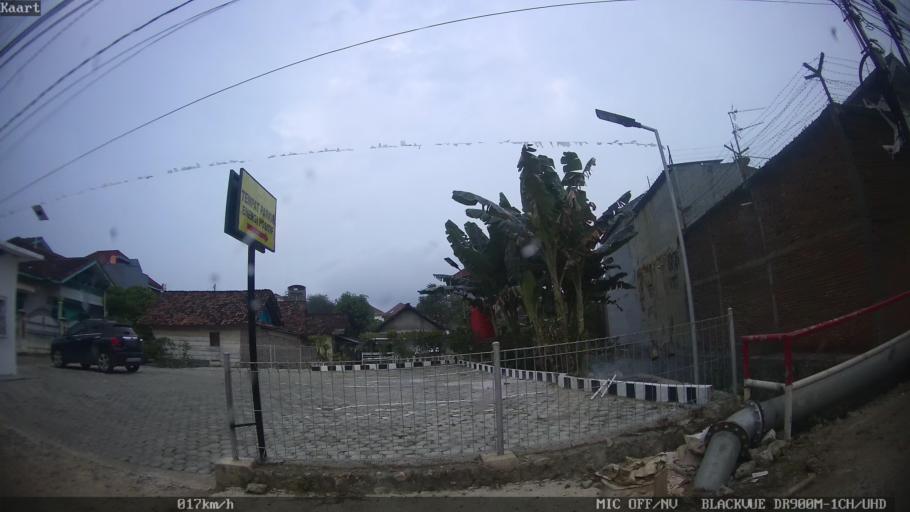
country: ID
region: Lampung
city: Kedaton
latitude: -5.3984
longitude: 105.2721
